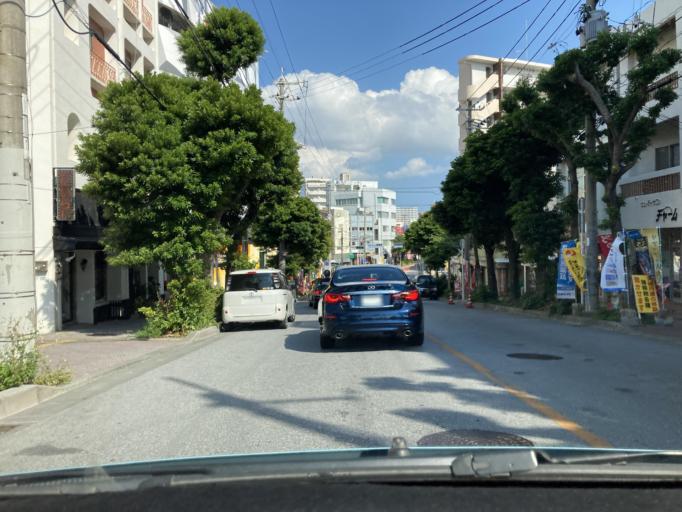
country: JP
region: Okinawa
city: Naha-shi
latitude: 26.2116
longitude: 127.6885
